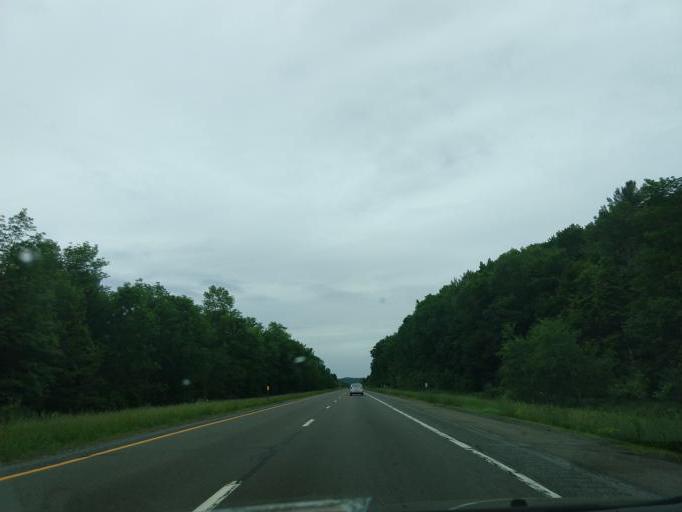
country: US
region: New York
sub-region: Broome County
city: Chenango Bridge
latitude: 42.2745
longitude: -75.9261
